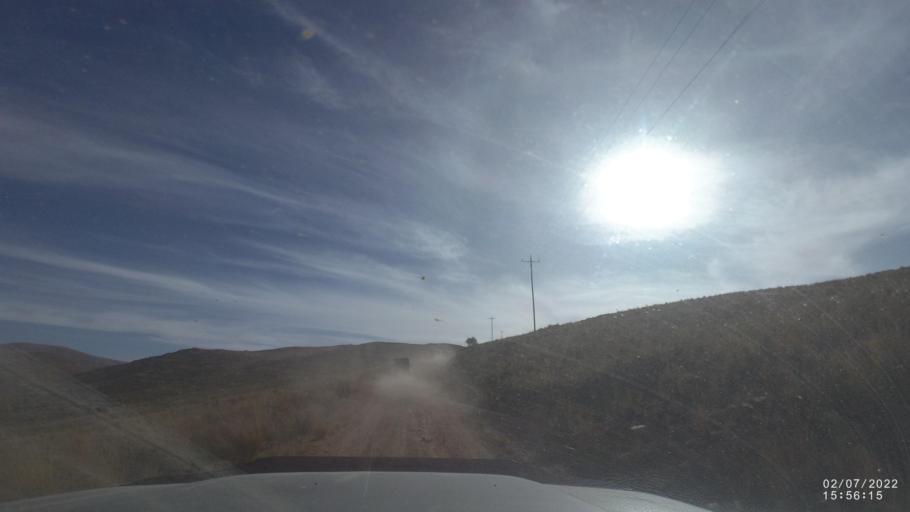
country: BO
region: Cochabamba
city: Irpa Irpa
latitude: -17.9093
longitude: -66.4241
